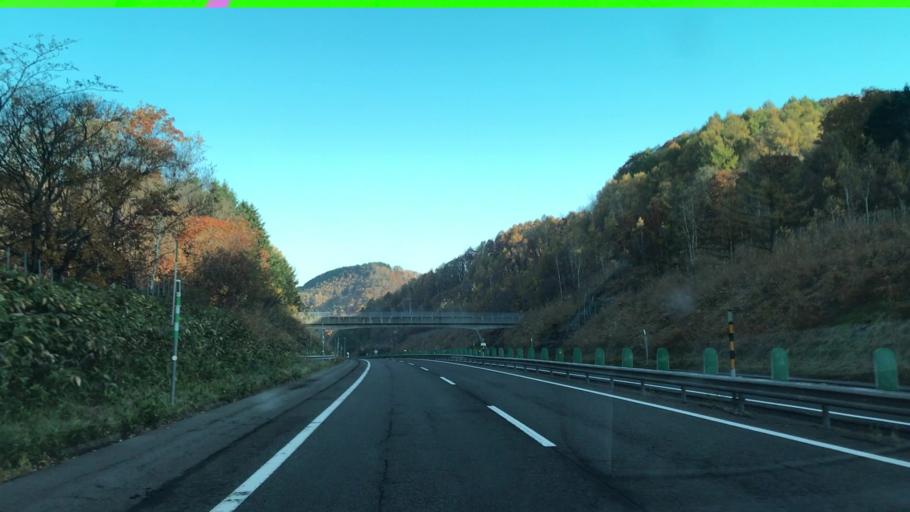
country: JP
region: Hokkaido
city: Sunagawa
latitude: 43.4097
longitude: 141.9087
